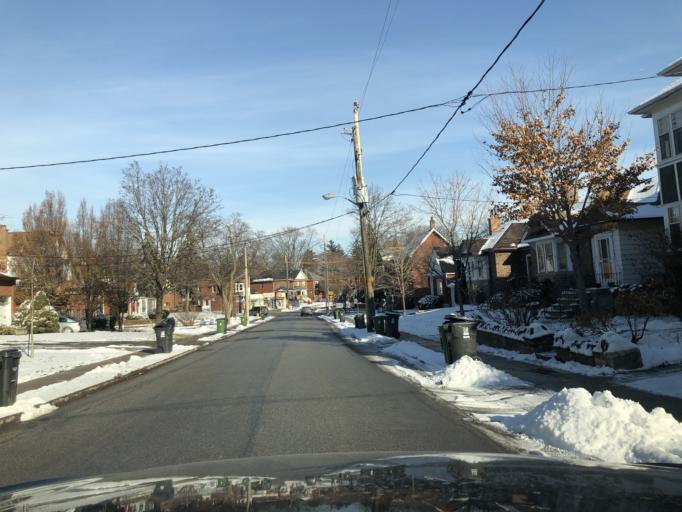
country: CA
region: Ontario
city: Etobicoke
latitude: 43.7051
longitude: -79.5164
